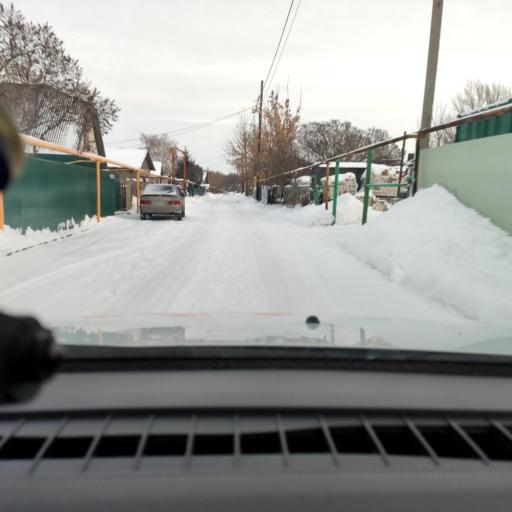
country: RU
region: Samara
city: Novokuybyshevsk
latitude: 53.0903
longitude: 50.0579
